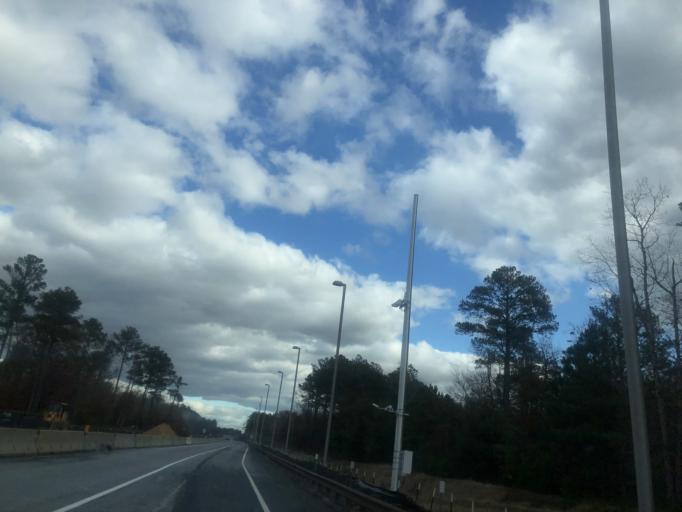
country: US
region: New Jersey
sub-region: Ocean County
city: Mystic Island
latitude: 39.6136
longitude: -74.4230
